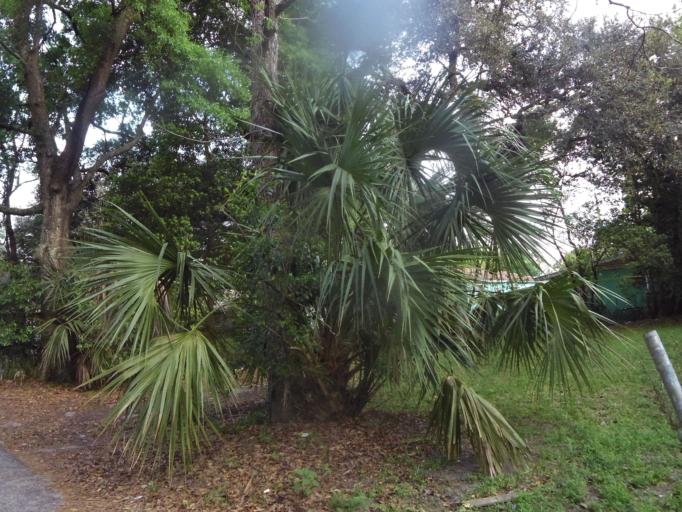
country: US
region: Florida
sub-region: Duval County
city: Jacksonville
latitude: 30.3608
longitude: -81.6348
